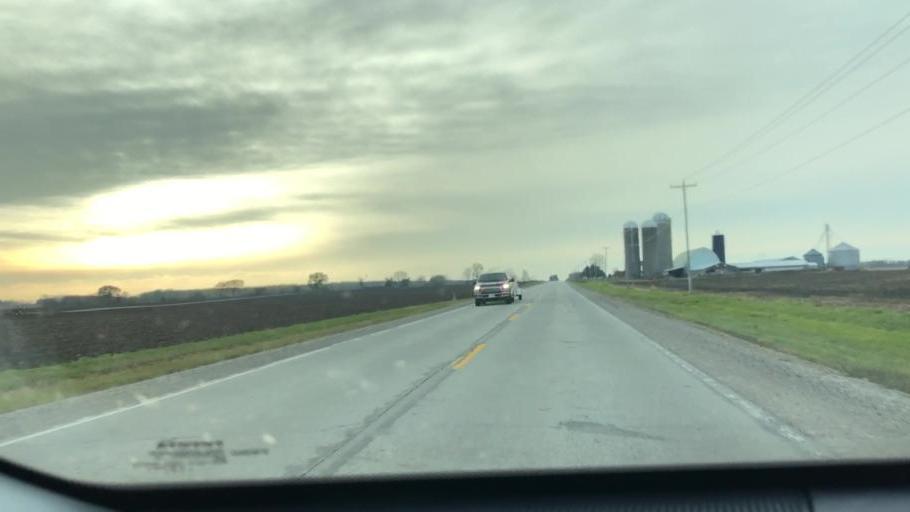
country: US
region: Wisconsin
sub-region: Outagamie County
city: Seymour
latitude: 44.4438
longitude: -88.2982
